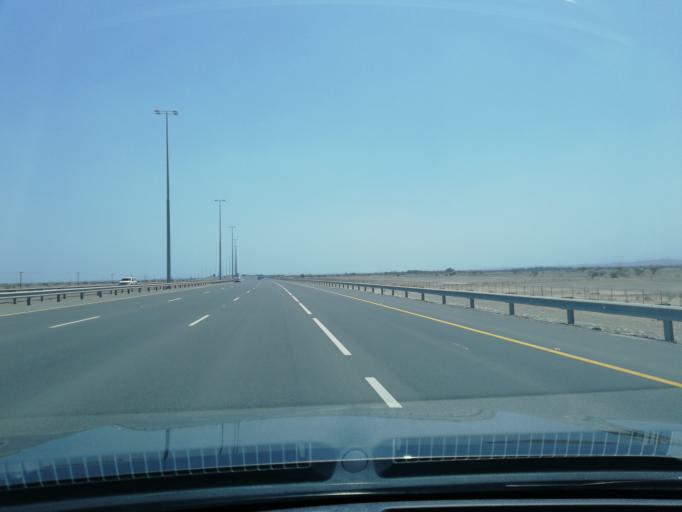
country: OM
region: Al Batinah
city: Barka'
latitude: 23.6183
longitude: 57.9258
